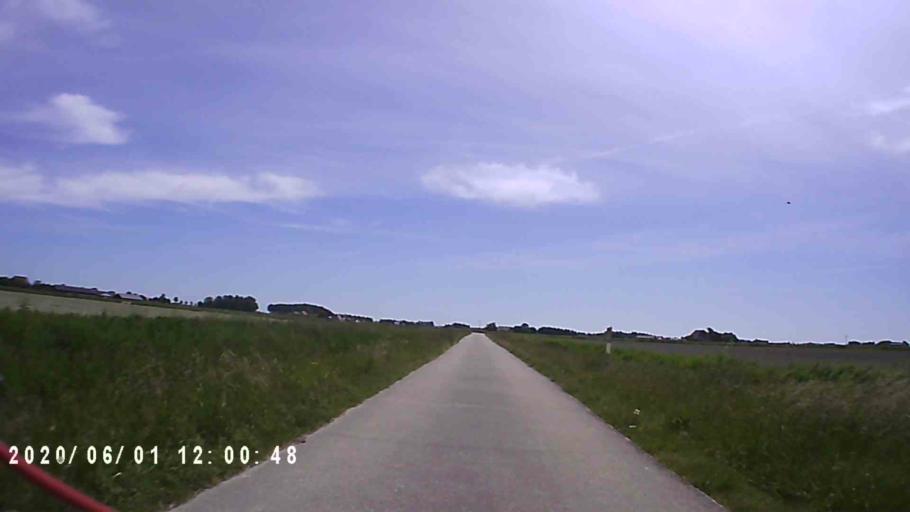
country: NL
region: Friesland
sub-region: Gemeente Harlingen
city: Harlingen
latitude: 53.1586
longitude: 5.4516
